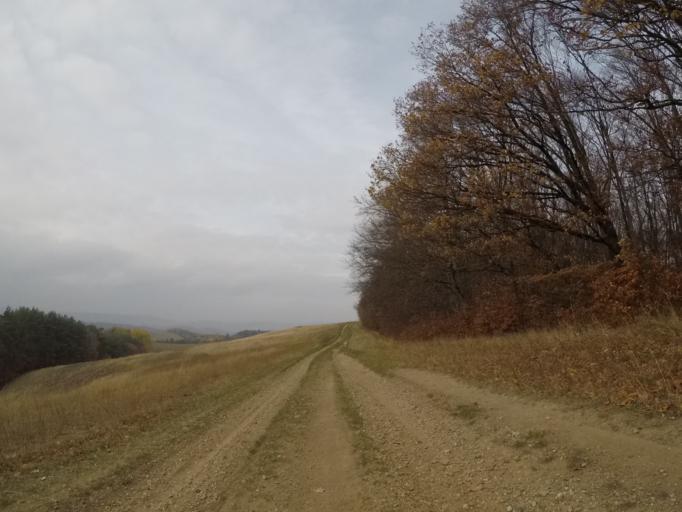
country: SK
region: Presovsky
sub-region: Okres Presov
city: Presov
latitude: 48.9315
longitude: 21.1305
